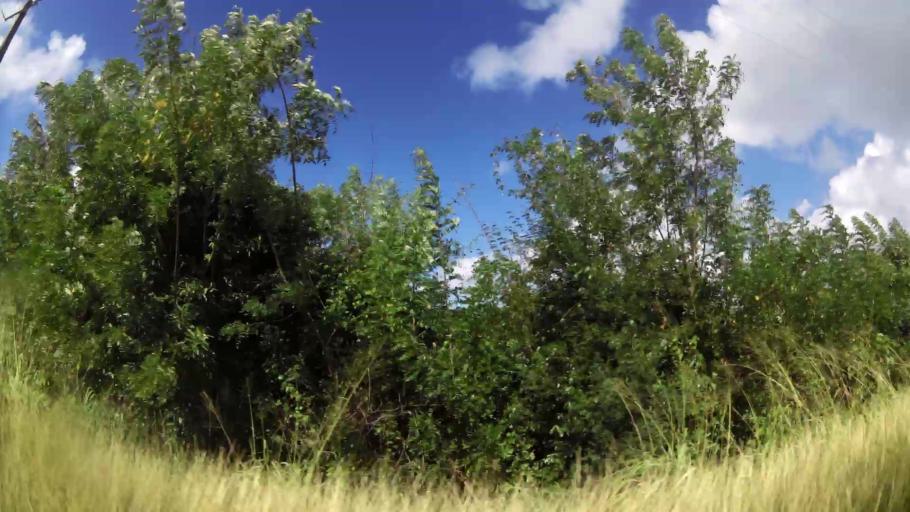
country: MQ
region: Martinique
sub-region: Martinique
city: Le Marin
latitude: 14.4113
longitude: -60.8793
